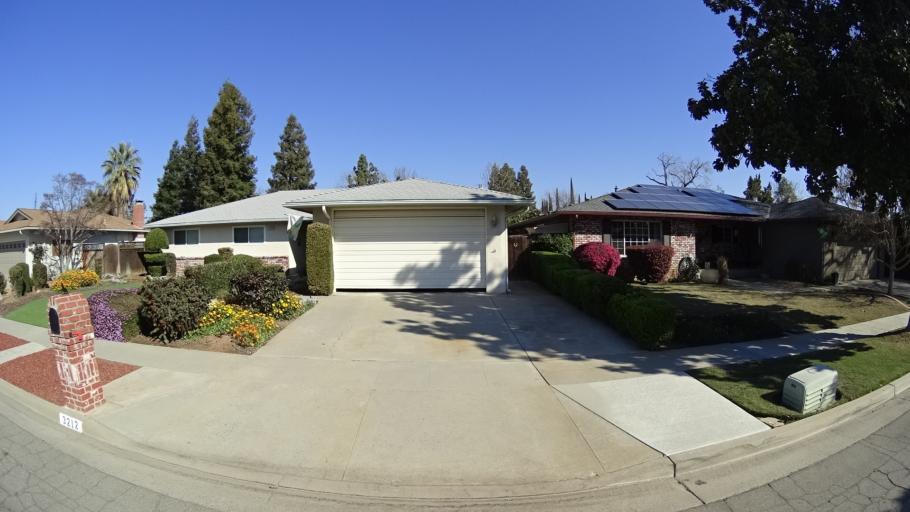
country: US
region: California
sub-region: Fresno County
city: Clovis
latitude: 36.8295
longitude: -119.7320
